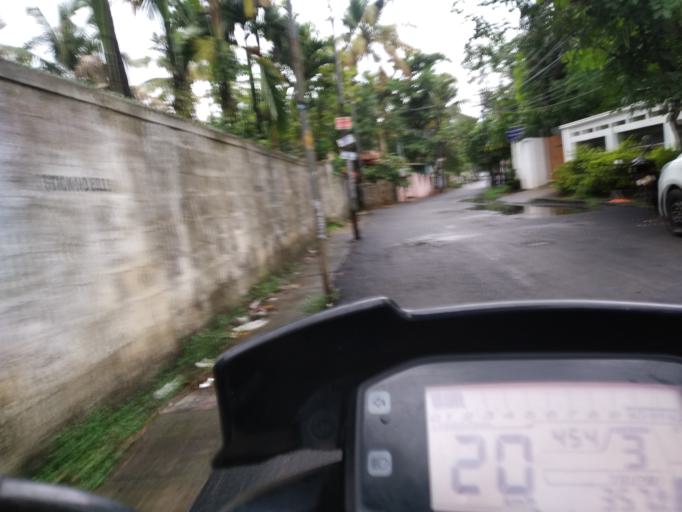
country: IN
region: Kerala
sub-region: Ernakulam
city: Cochin
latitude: 9.9748
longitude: 76.3084
